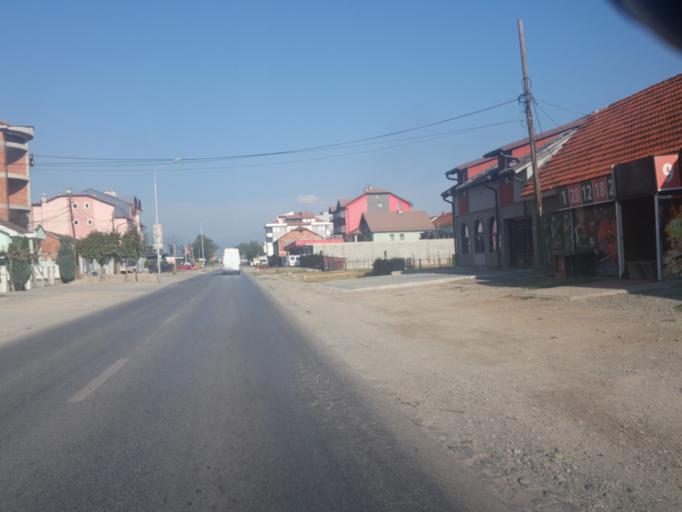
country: XK
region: Gjakova
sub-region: Komuna e Gjakoves
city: Gjakove
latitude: 42.4028
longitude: 20.4129
